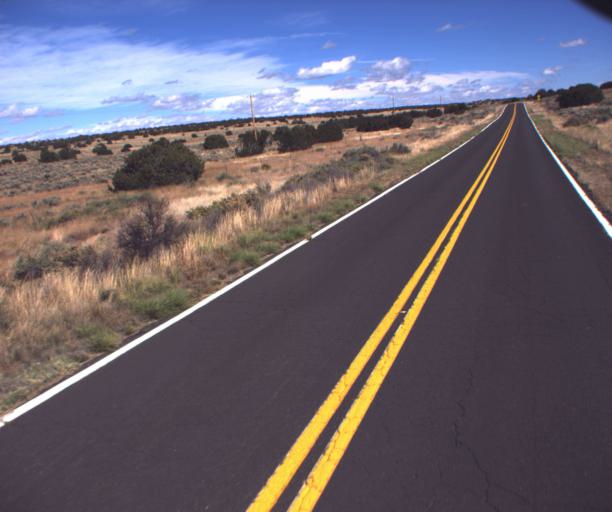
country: US
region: Arizona
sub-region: Apache County
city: Houck
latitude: 34.9250
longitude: -109.2030
